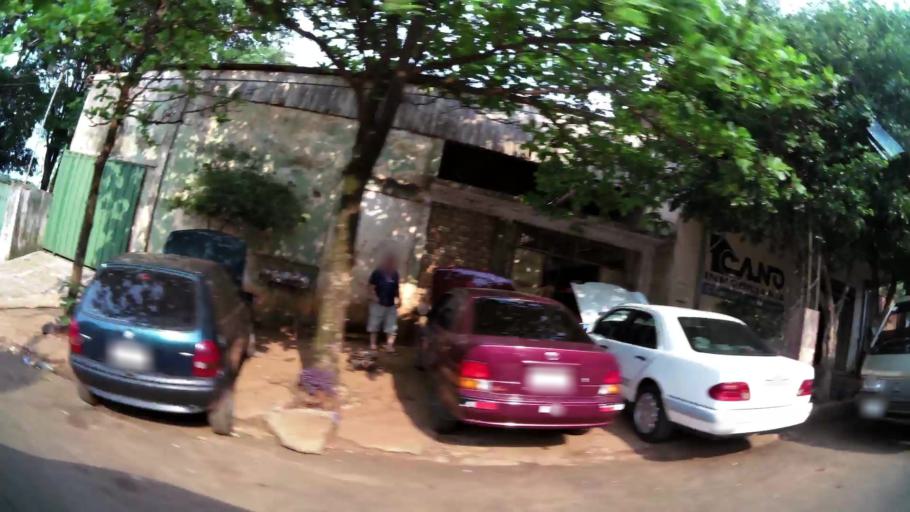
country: PY
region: Alto Parana
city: Ciudad del Este
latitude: -25.4988
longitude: -54.6602
